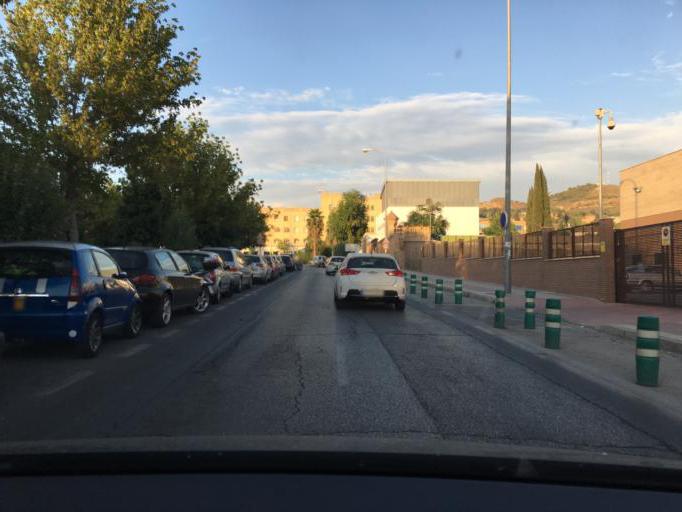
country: ES
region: Andalusia
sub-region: Provincia de Granada
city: Granada
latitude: 37.1918
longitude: -3.6070
